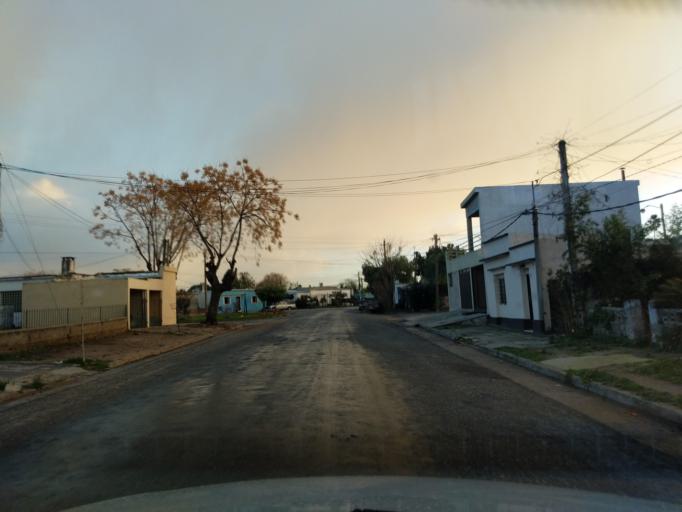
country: UY
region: Florida
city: Florida
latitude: -34.1070
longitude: -56.2102
